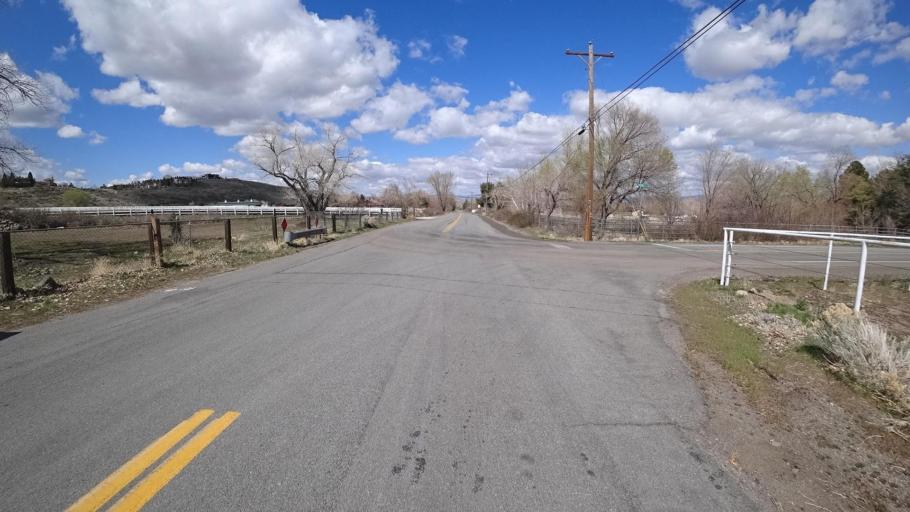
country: US
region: Nevada
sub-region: Washoe County
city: Reno
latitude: 39.4295
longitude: -119.7892
